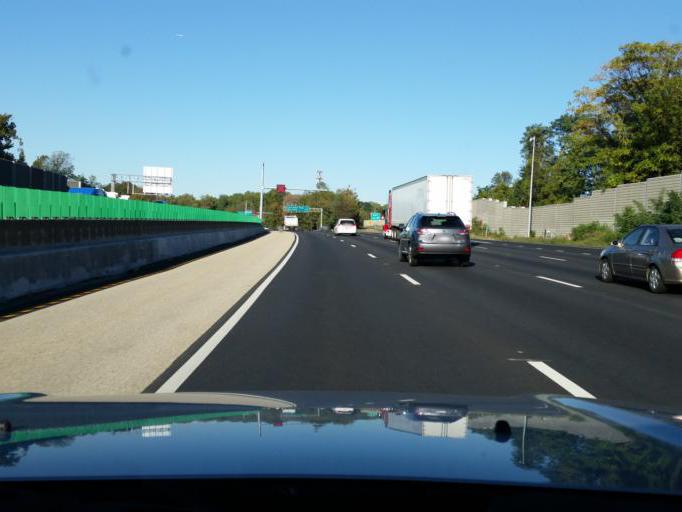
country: US
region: Virginia
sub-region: Fairfax County
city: McLean
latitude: 38.9513
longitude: -77.1968
